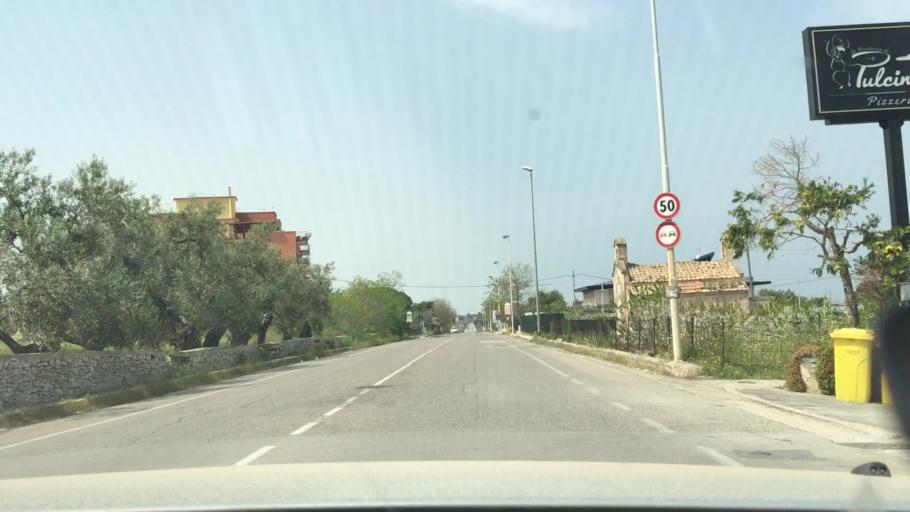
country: IT
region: Apulia
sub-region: Provincia di Barletta - Andria - Trani
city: Capirro
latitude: 41.2564
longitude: 16.4573
